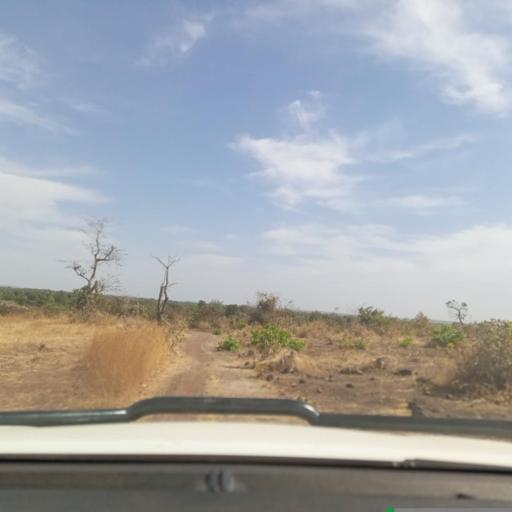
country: ML
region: Koulikoro
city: Kati
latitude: 12.7489
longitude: -8.2424
